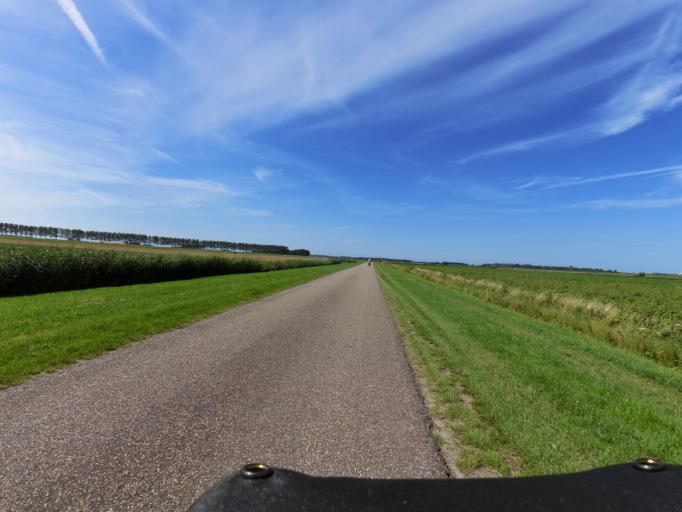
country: NL
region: South Holland
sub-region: Gemeente Goeree-Overflakkee
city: Dirksland
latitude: 51.8018
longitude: 4.0655
